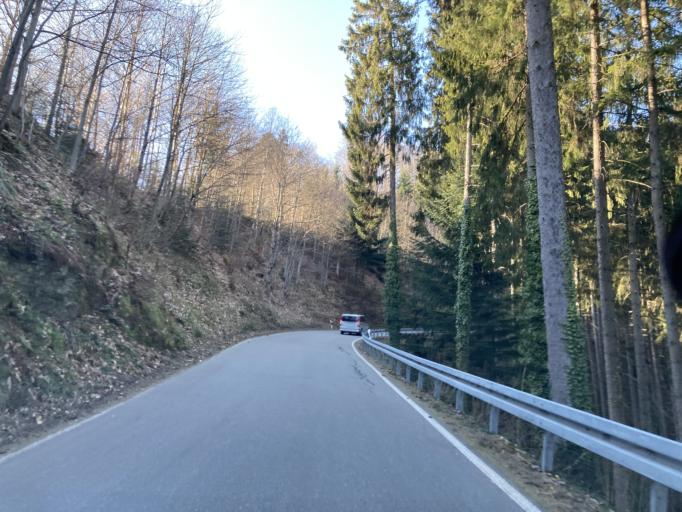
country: DE
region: Baden-Wuerttemberg
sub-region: Freiburg Region
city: Oppenau
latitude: 48.4819
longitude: 8.2043
